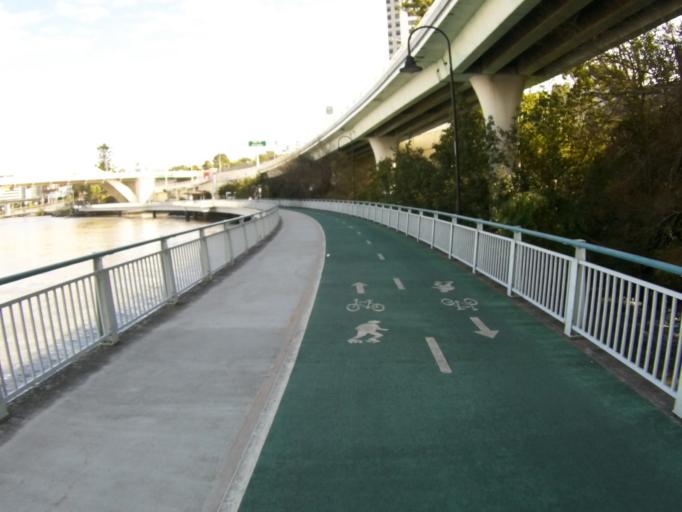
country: AU
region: Queensland
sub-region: Brisbane
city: Spring Hill
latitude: -27.4678
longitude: 153.0174
